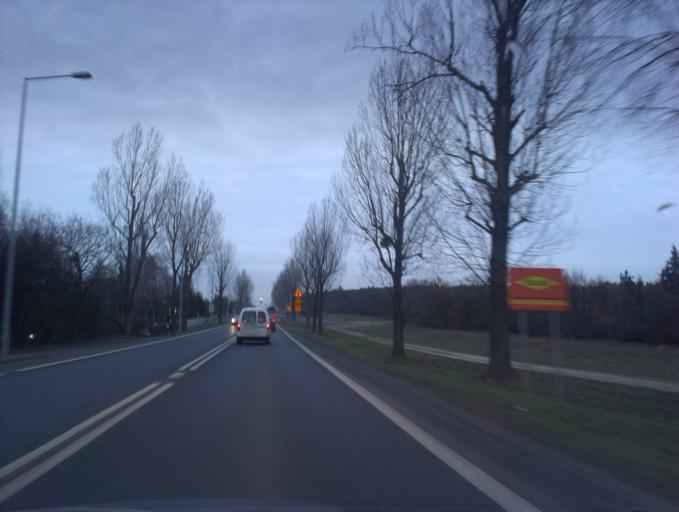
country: PL
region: Greater Poland Voivodeship
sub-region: Powiat poznanski
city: Zlotniki
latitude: 52.4953
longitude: 16.8426
